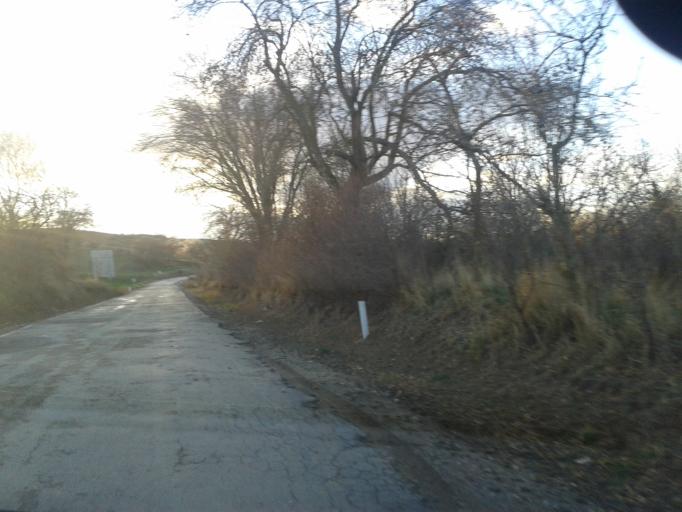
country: ES
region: Aragon
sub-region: Provincia de Teruel
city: Lagueruela
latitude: 41.0404
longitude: -1.1944
